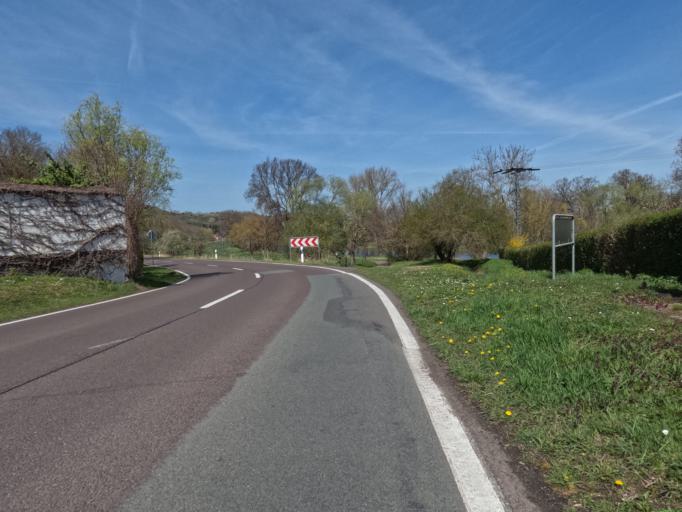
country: DE
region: Saxony-Anhalt
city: Beesenstedt
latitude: 51.5798
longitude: 11.7653
